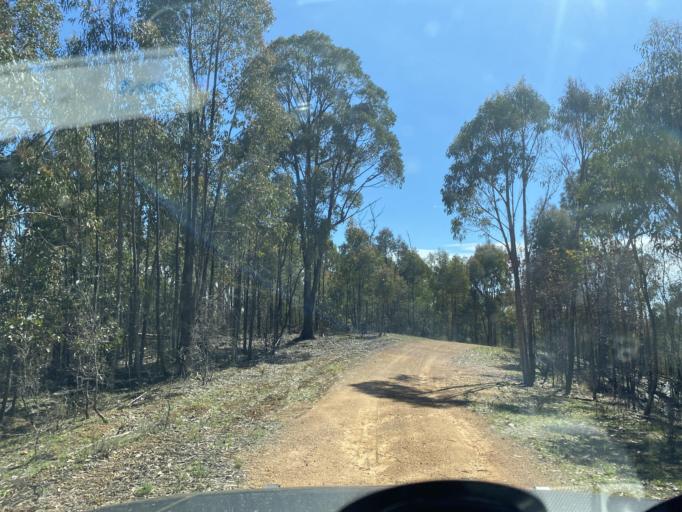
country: AU
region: Victoria
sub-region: Benalla
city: Benalla
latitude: -36.7386
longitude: 146.1797
